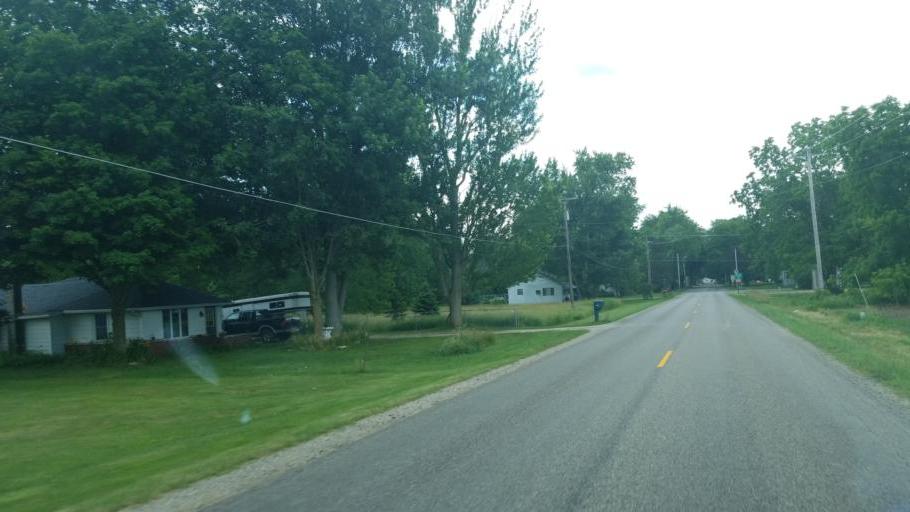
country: US
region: Michigan
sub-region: Eaton County
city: Bellevue
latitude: 42.4525
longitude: -85.0183
